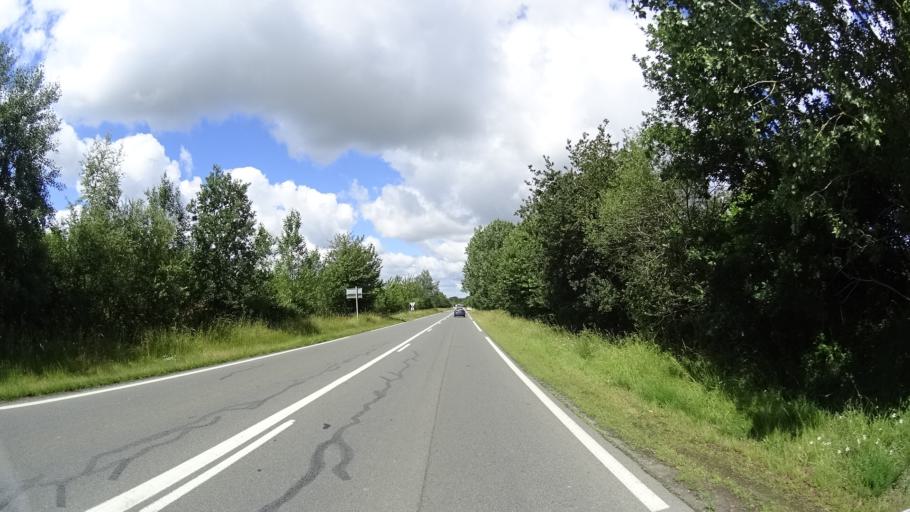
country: FR
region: Brittany
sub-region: Departement d'Ille-et-Vilaine
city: Le Rheu
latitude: 48.1170
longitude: -1.8077
